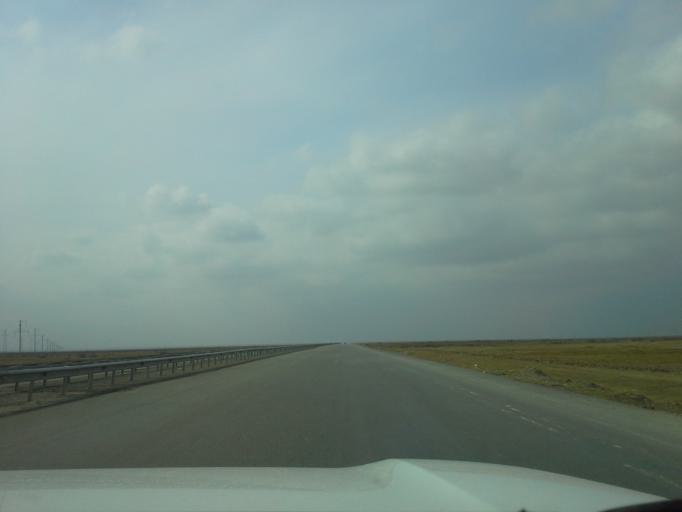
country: IR
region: Razavi Khorasan
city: Kalat-e Naderi
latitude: 37.2141
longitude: 60.0025
